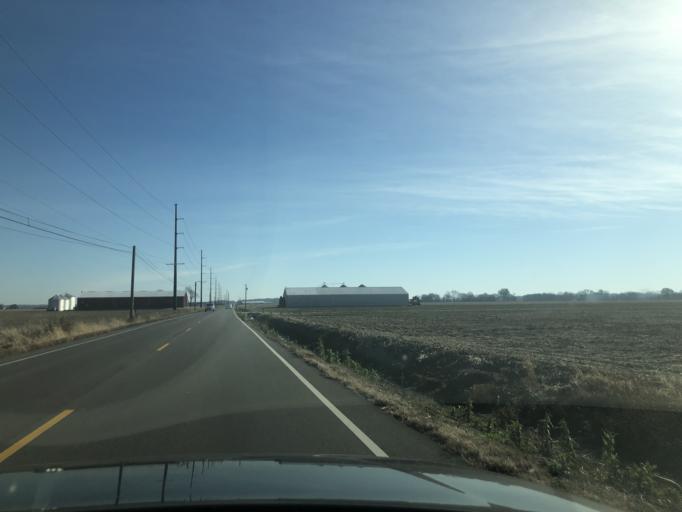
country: US
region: Indiana
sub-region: Vanderburgh County
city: Melody Hill
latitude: 37.9912
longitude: -87.4585
